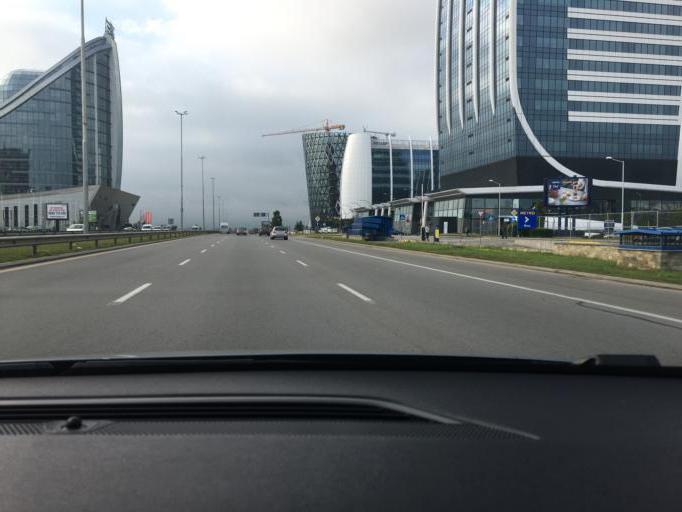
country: BG
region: Sofia-Capital
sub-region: Stolichna Obshtina
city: Sofia
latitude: 42.6481
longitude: 23.3953
